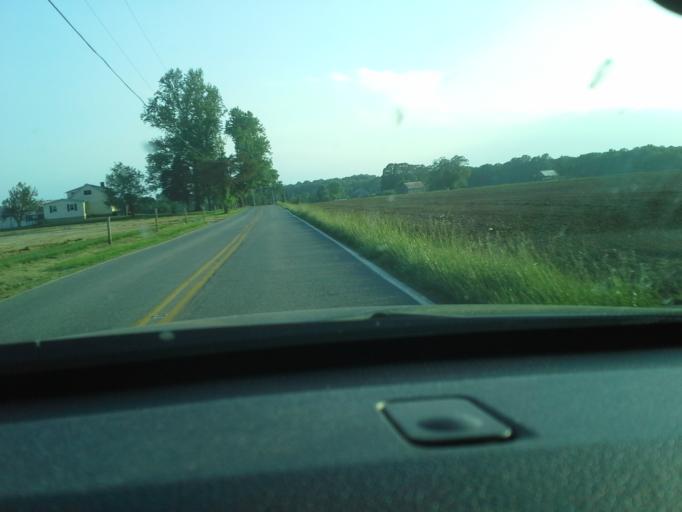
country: US
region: Maryland
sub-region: Anne Arundel County
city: Deale
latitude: 38.8109
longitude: -76.5527
